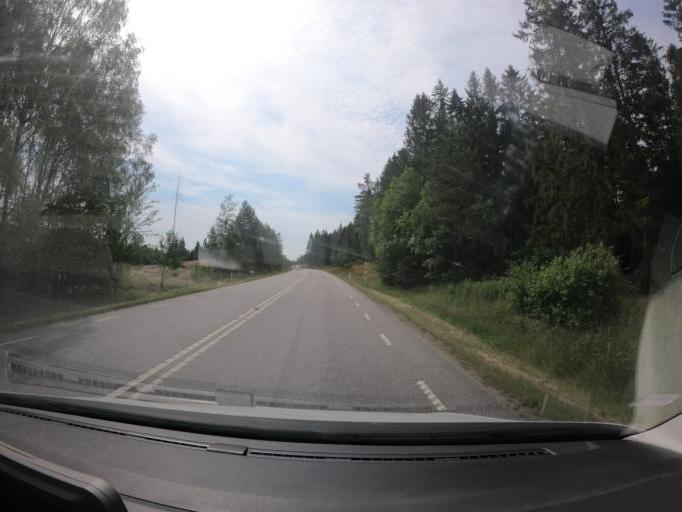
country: SE
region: Skane
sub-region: Hassleholms Kommun
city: Bjarnum
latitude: 56.2335
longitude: 13.7138
